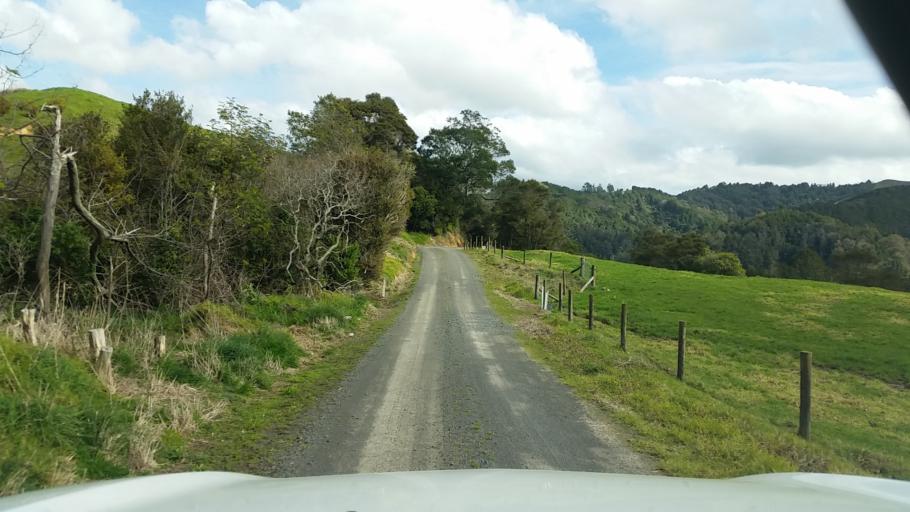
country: NZ
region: Waikato
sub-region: Hauraki District
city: Ngatea
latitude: -37.4649
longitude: 175.4629
